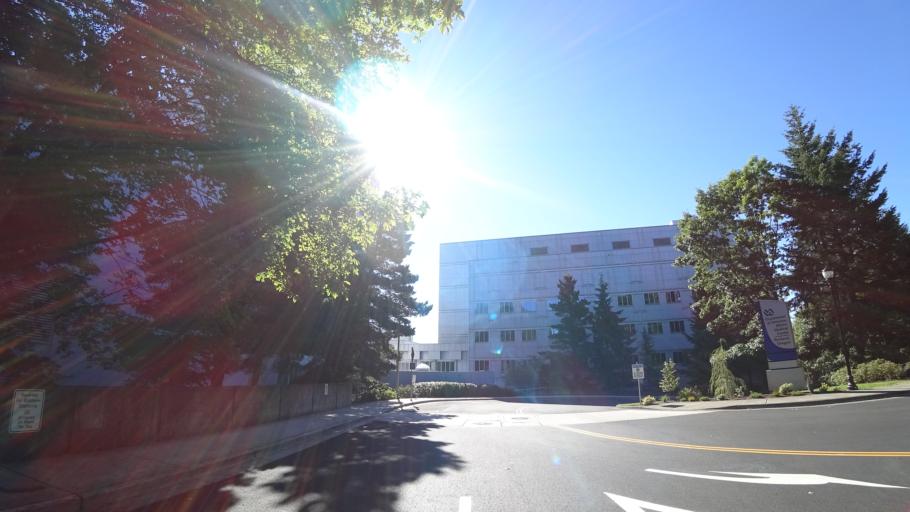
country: US
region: Oregon
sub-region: Multnomah County
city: Portland
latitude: 45.4967
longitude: -122.6849
